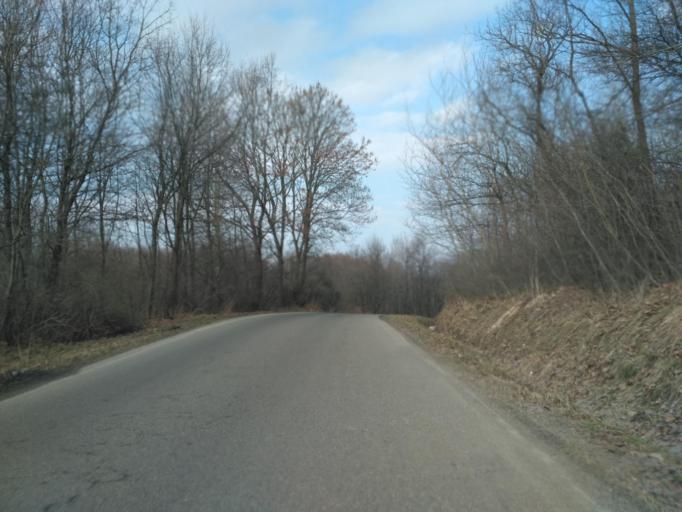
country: PL
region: Subcarpathian Voivodeship
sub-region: Powiat brzozowski
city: Gorki
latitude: 49.6631
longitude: 22.0295
